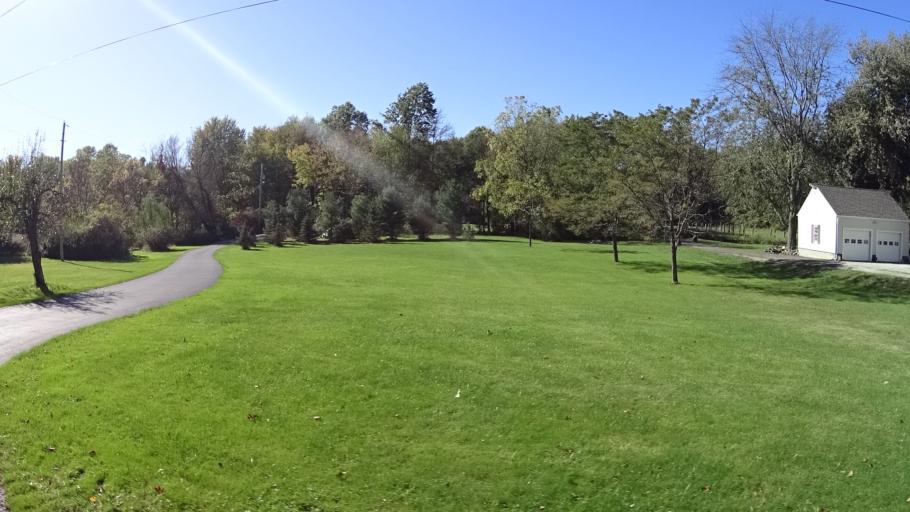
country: US
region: Ohio
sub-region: Lorain County
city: Amherst
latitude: 41.3732
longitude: -82.1930
